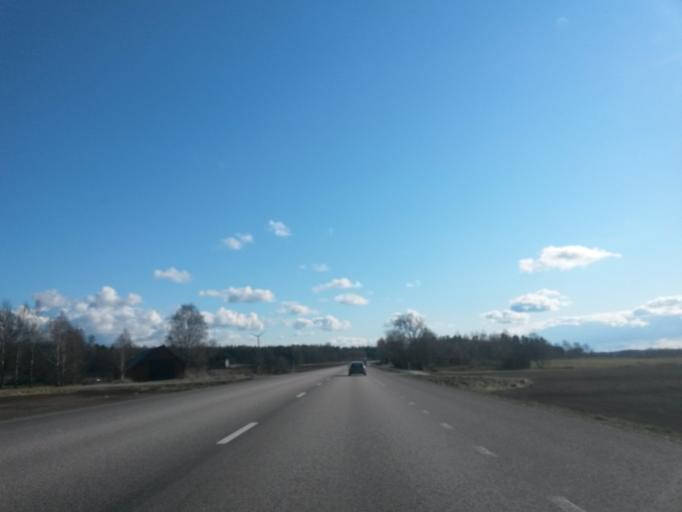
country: SE
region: Vaestra Goetaland
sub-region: Vargarda Kommun
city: Vargarda
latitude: 58.1349
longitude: 12.8601
